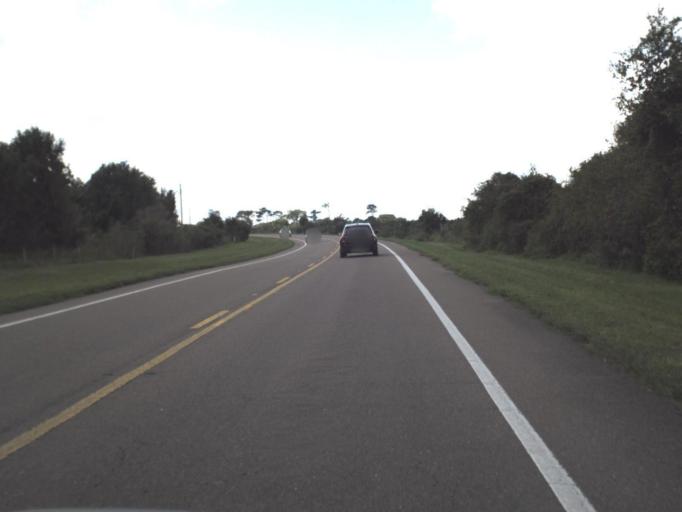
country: US
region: Florida
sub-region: DeSoto County
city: Arcadia
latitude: 27.2941
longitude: -82.0610
